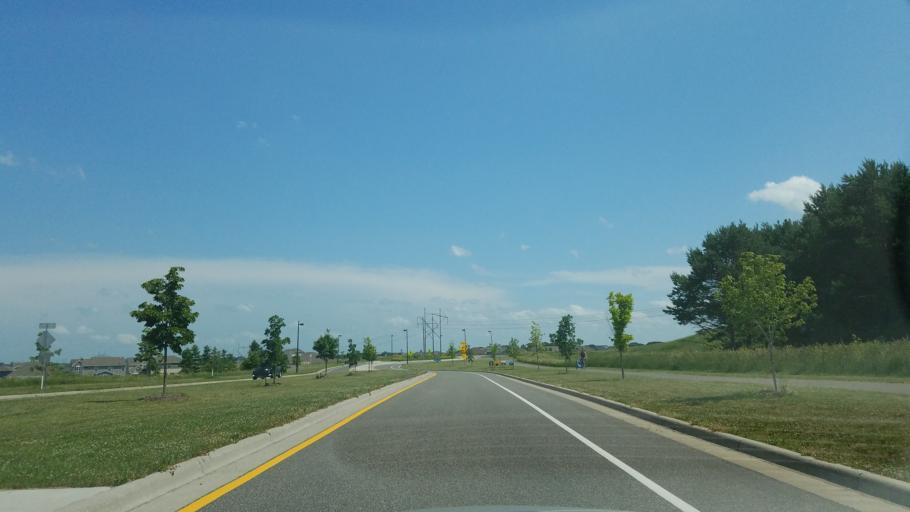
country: US
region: Minnesota
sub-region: Washington County
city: Woodbury
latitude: 44.8849
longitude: -92.9270
